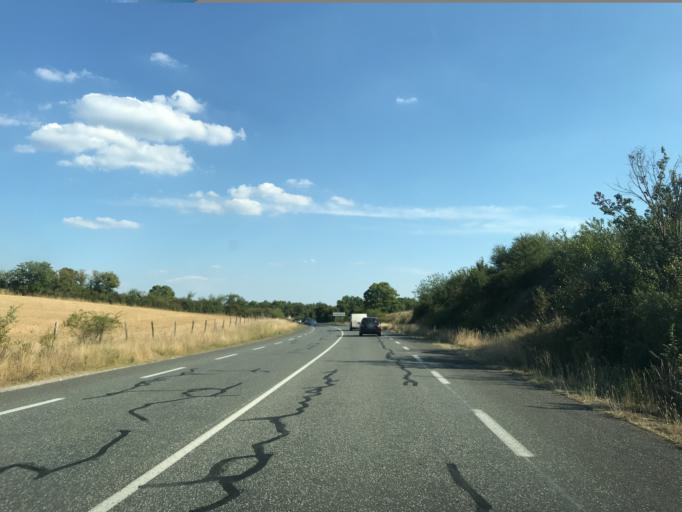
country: FR
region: Midi-Pyrenees
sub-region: Departement du Lot
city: Gramat
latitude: 44.6891
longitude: 1.5999
